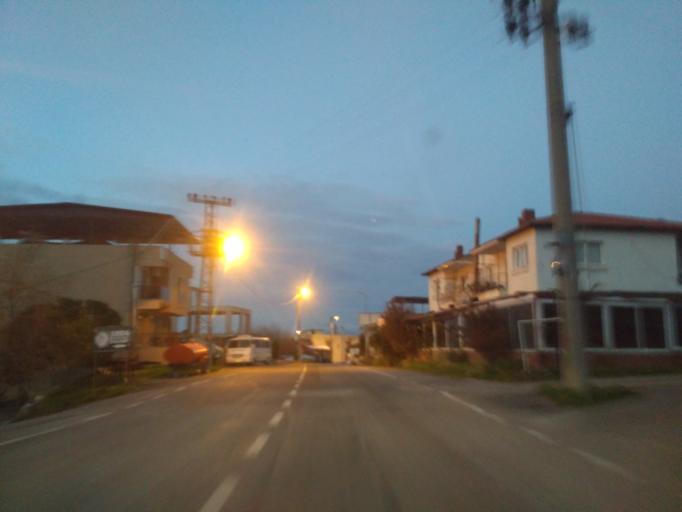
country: TR
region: Izmir
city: Buca
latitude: 38.3662
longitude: 27.2732
